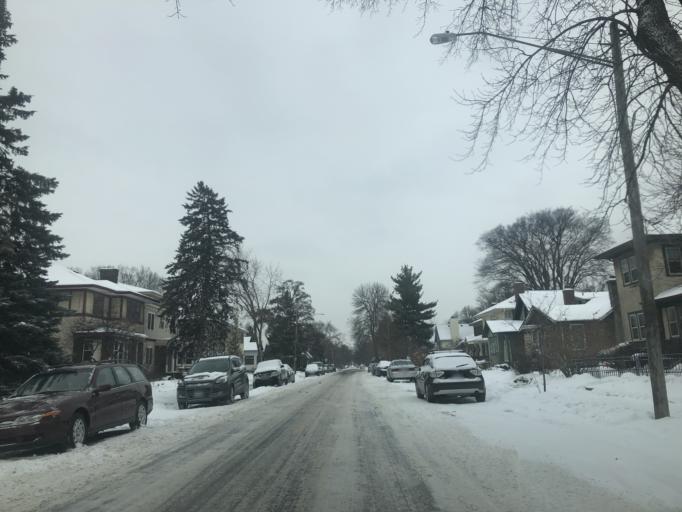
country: US
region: Minnesota
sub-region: Hennepin County
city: Richfield
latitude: 44.9281
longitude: -93.2844
